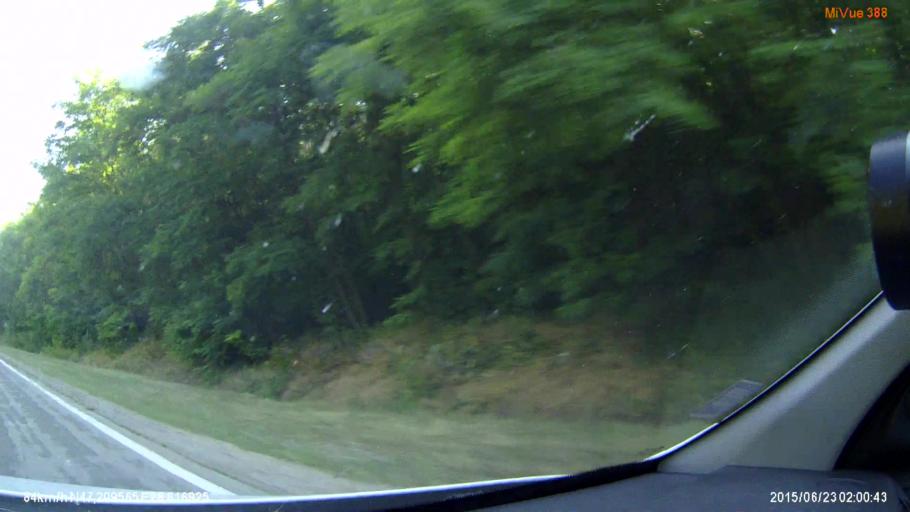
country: MD
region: Straseni
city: Straseni
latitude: 47.2099
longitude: 28.6172
